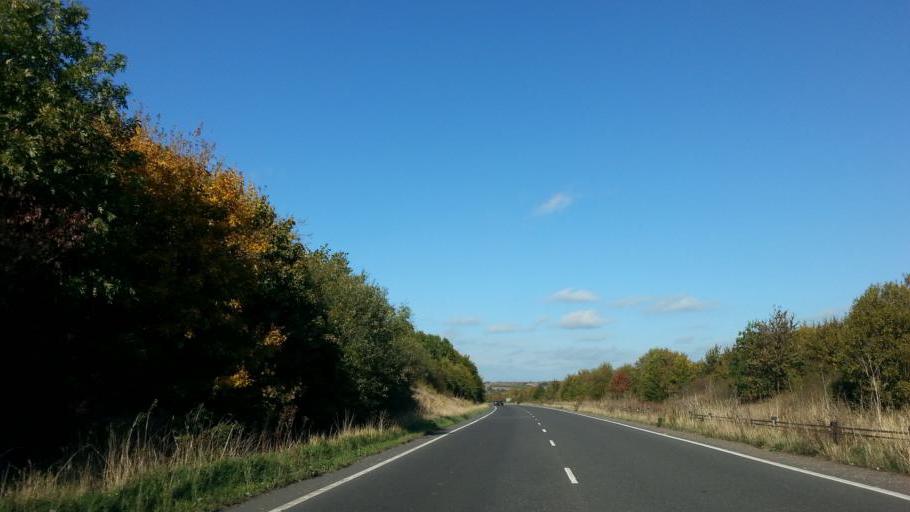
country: GB
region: England
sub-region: Northamptonshire
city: Higham Ferrers
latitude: 52.3122
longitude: -0.5865
